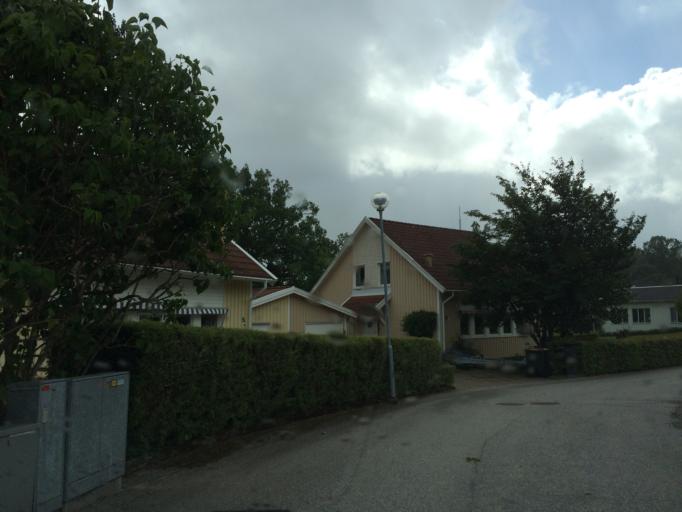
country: SE
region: Vaestra Goetaland
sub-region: Trollhattan
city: Trollhattan
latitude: 58.2960
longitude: 12.2788
